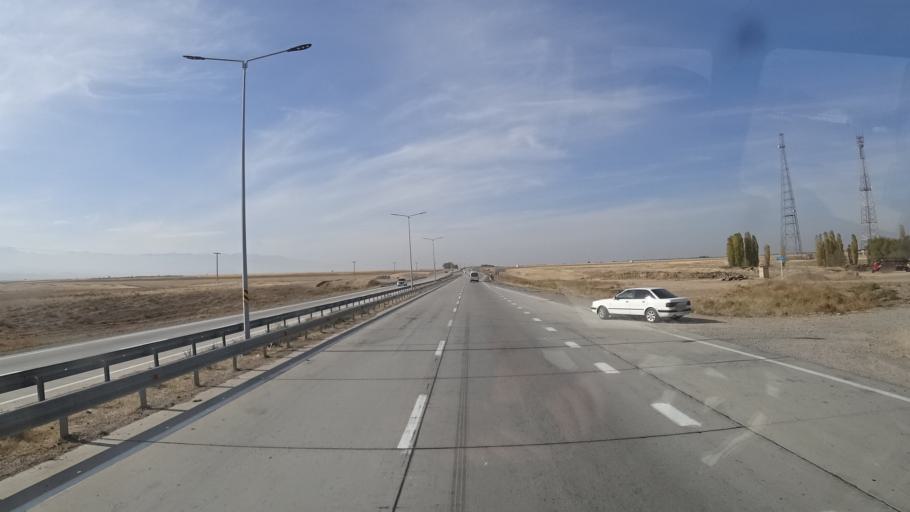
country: KZ
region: Zhambyl
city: Merke
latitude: 42.8896
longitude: 72.9831
